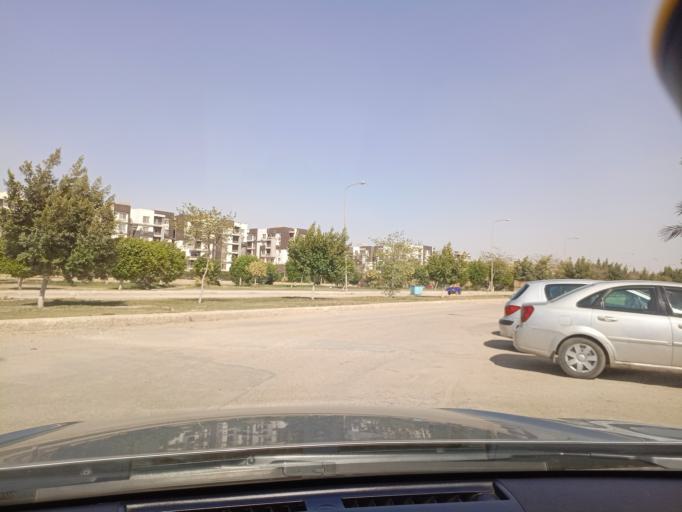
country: EG
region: Muhafazat al Qalyubiyah
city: Al Khankah
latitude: 30.2301
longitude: 31.4416
